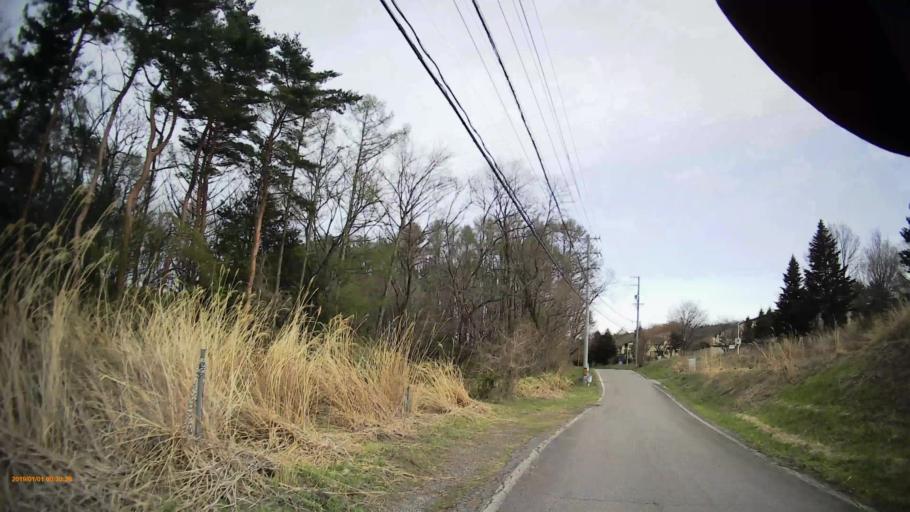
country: JP
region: Nagano
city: Chino
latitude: 35.9350
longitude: 138.2010
